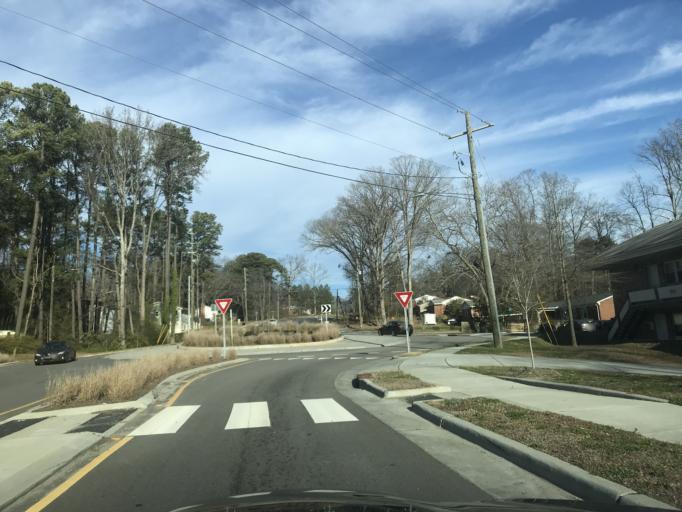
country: US
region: North Carolina
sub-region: Wake County
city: Cary
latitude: 35.7732
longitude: -78.7365
